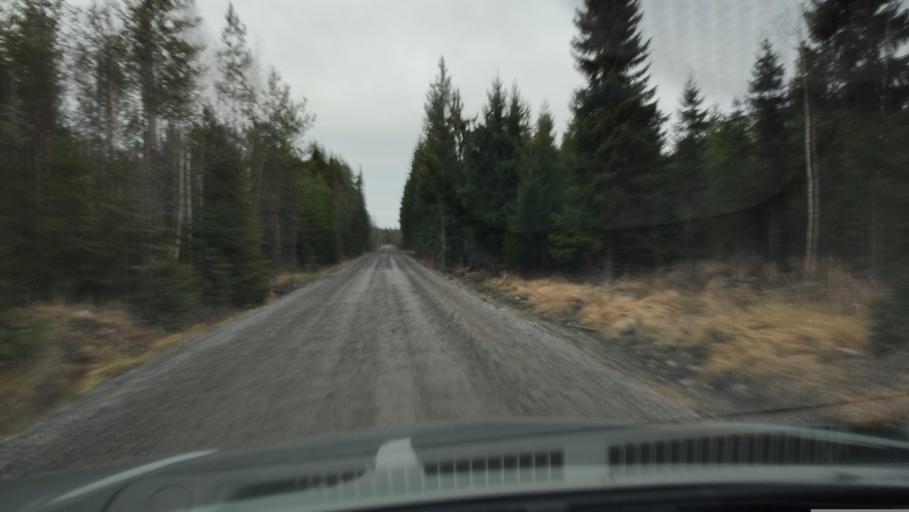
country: FI
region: Southern Ostrobothnia
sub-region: Suupohja
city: Karijoki
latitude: 62.1939
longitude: 21.5754
